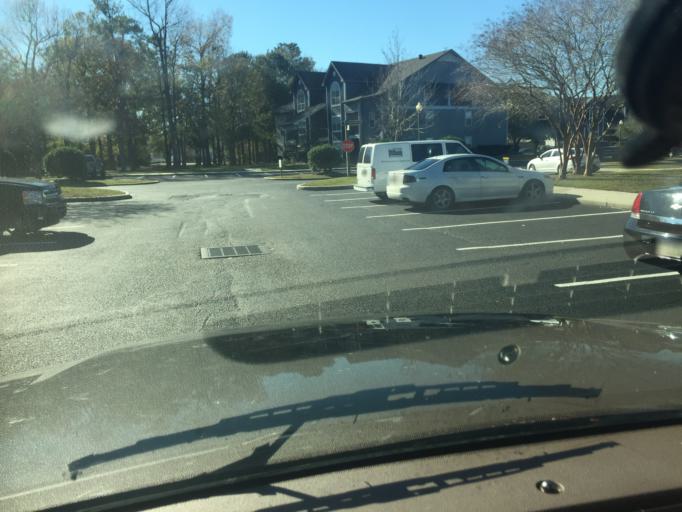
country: US
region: Louisiana
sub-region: Saint Tammany Parish
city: Slidell
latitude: 30.3125
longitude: -89.7472
